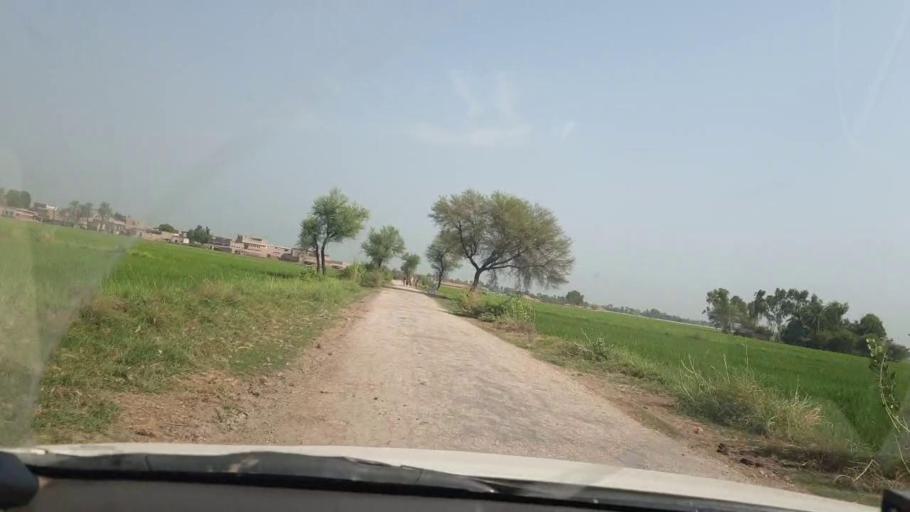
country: PK
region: Sindh
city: Chak
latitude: 27.8348
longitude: 68.7989
